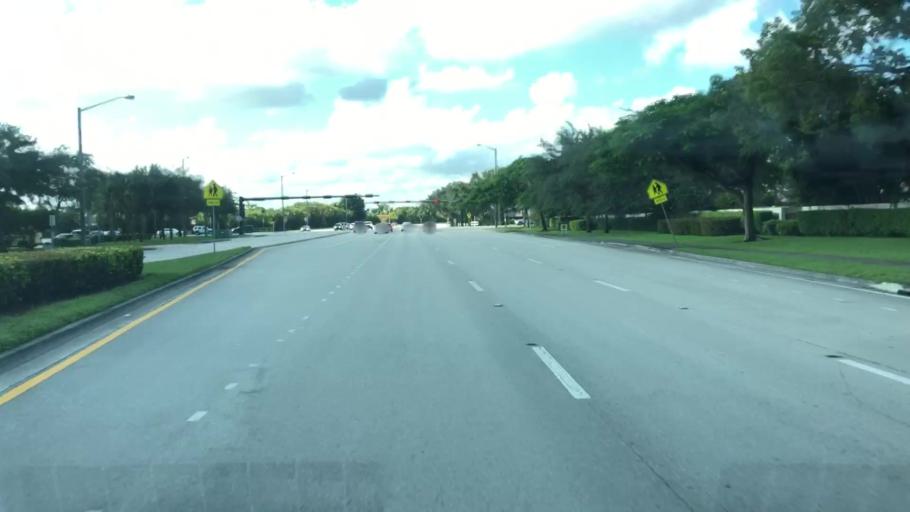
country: US
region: Florida
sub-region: Broward County
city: Coral Springs
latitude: 26.2422
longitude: -80.2690
